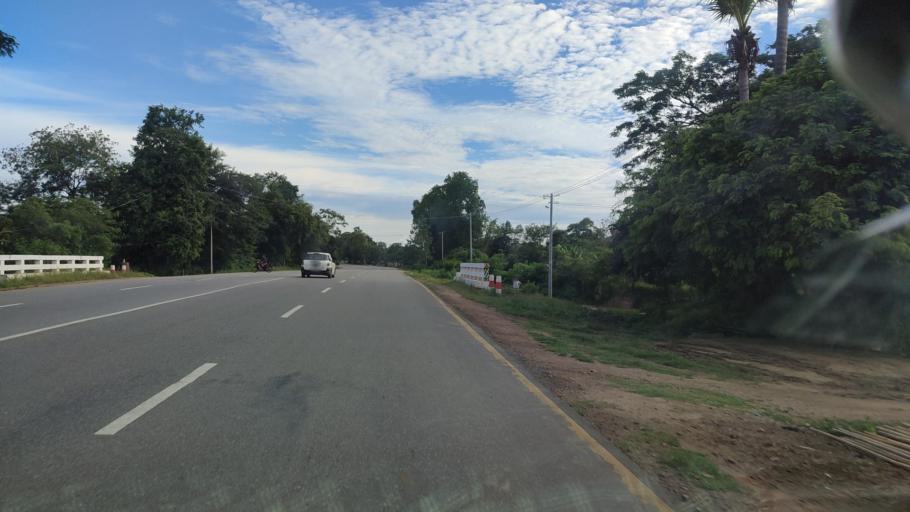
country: MM
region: Mandalay
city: Yamethin
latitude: 20.2119
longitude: 96.1818
